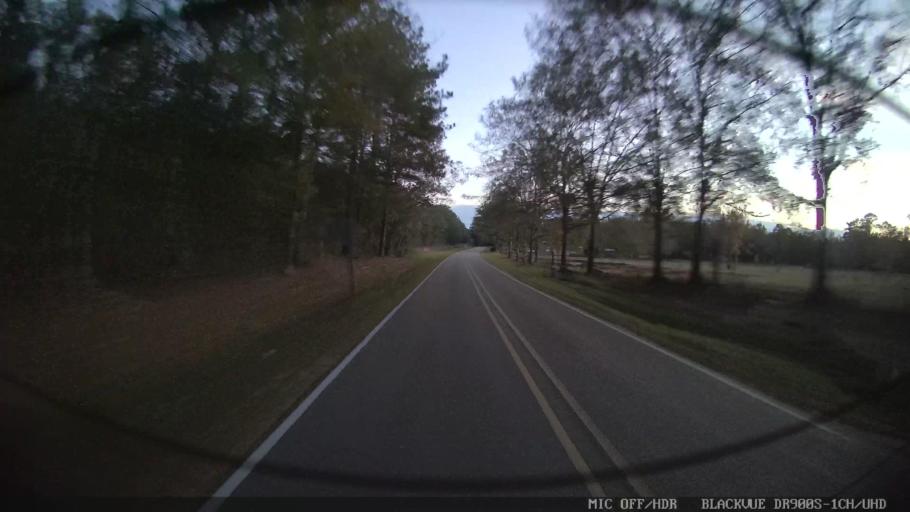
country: US
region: Mississippi
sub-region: Perry County
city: New Augusta
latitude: 31.0908
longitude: -89.1883
